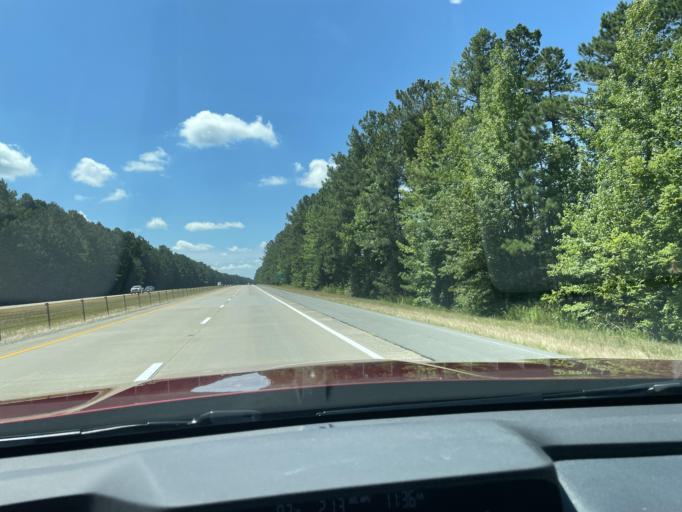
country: US
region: Arkansas
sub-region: Jefferson County
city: Redfield
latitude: 34.4302
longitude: -92.1938
